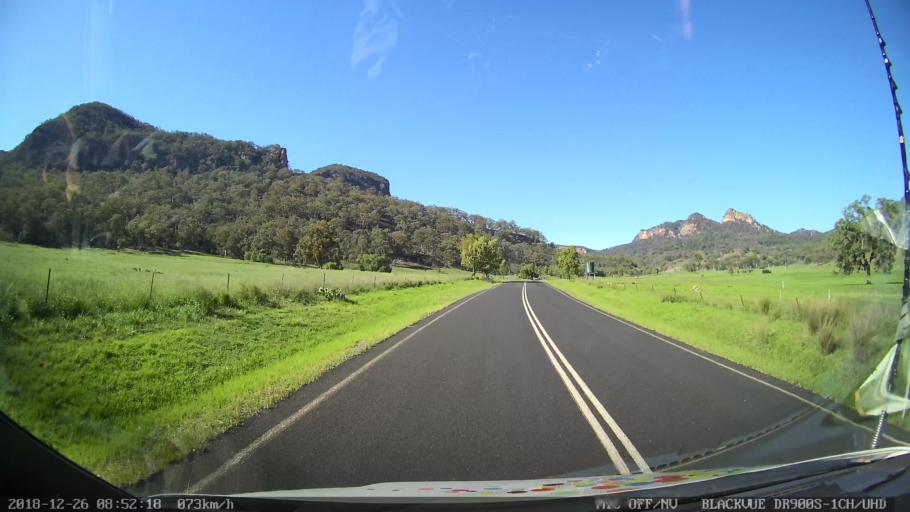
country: AU
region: New South Wales
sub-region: Mid-Western Regional
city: Kandos
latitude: -32.5953
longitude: 150.0867
